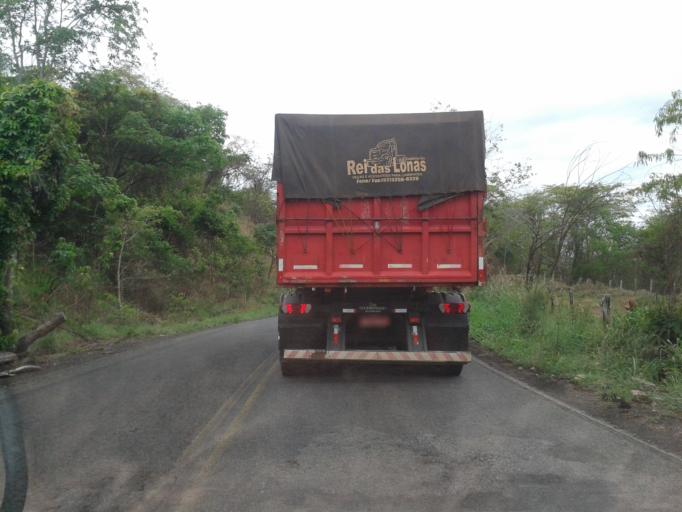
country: BR
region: Goias
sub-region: Caldas Novas
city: Caldas Novas
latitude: -18.0623
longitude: -48.6915
